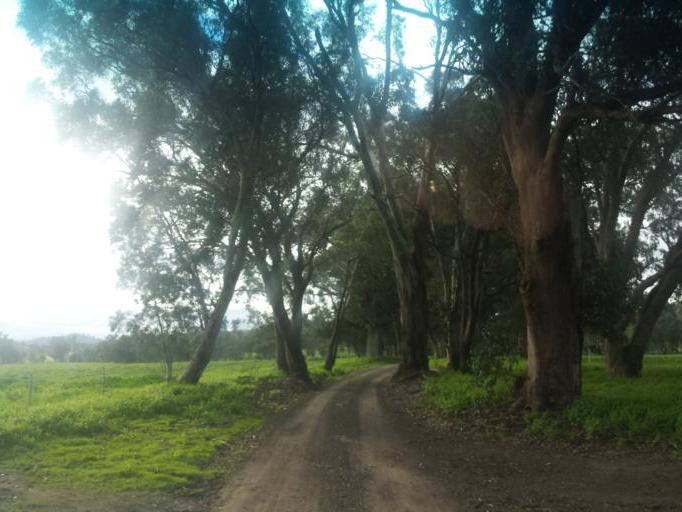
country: AU
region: Victoria
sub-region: Murrindindi
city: Kinglake West
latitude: -37.0414
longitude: 145.2501
